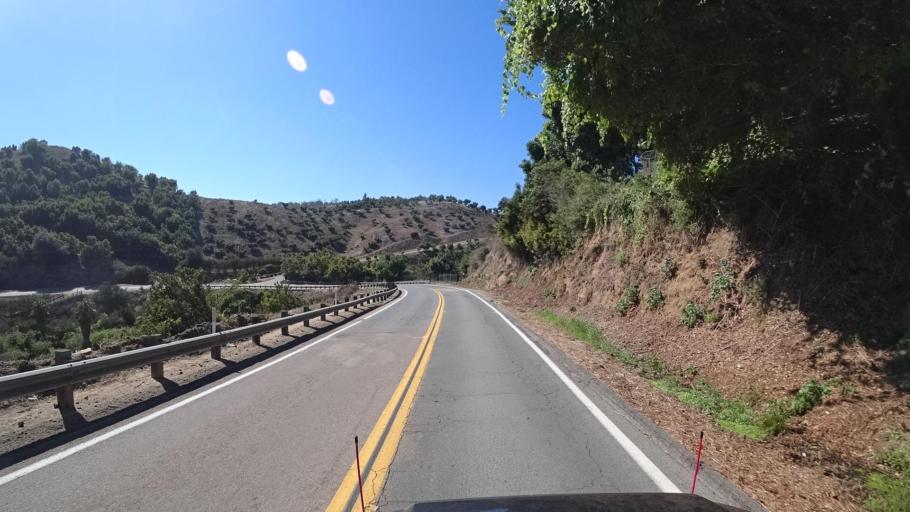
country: US
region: California
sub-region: San Diego County
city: Hidden Meadows
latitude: 33.2629
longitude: -117.1406
